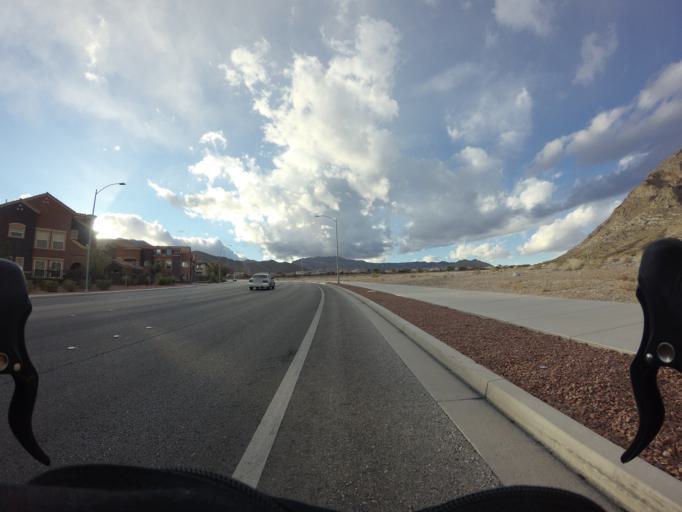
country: US
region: Nevada
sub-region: Clark County
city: Summerlin South
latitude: 36.2329
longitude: -115.3154
